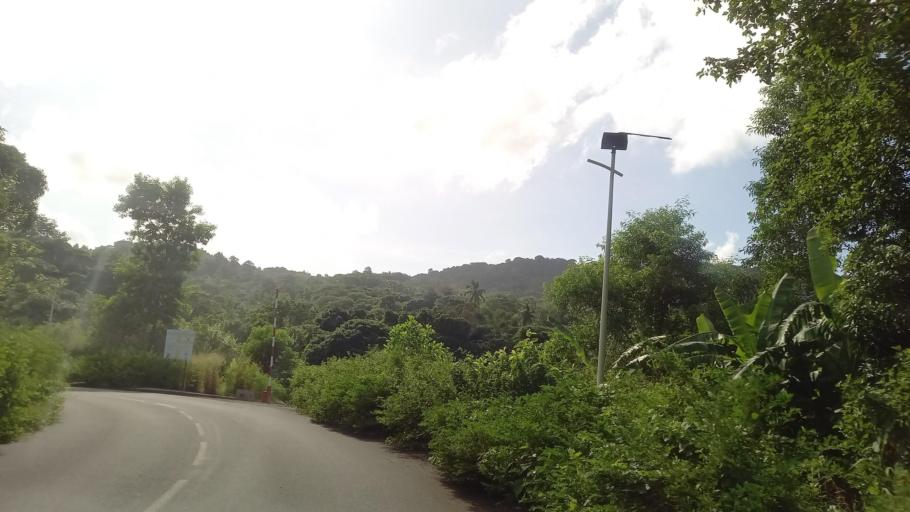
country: YT
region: Kani-Keli
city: Kani Keli
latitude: -12.9864
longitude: 45.1342
